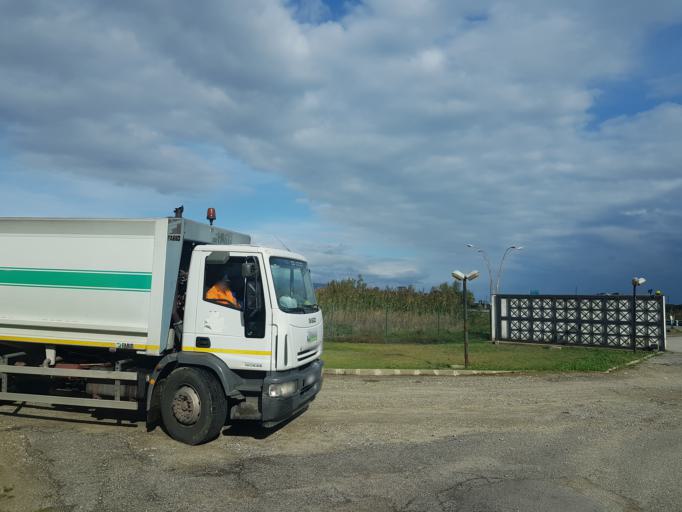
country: IT
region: Calabria
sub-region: Provincia di Cosenza
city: Sibari
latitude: 39.7268
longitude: 16.4959
